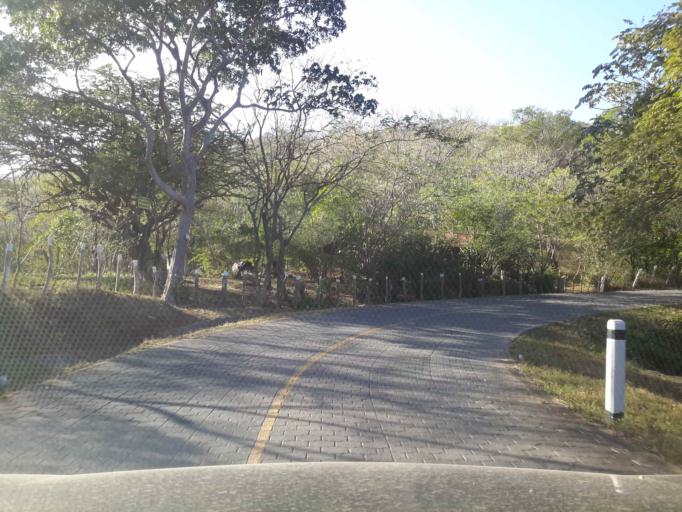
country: NI
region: Rivas
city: San Juan del Sur
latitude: 11.2216
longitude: -85.8159
